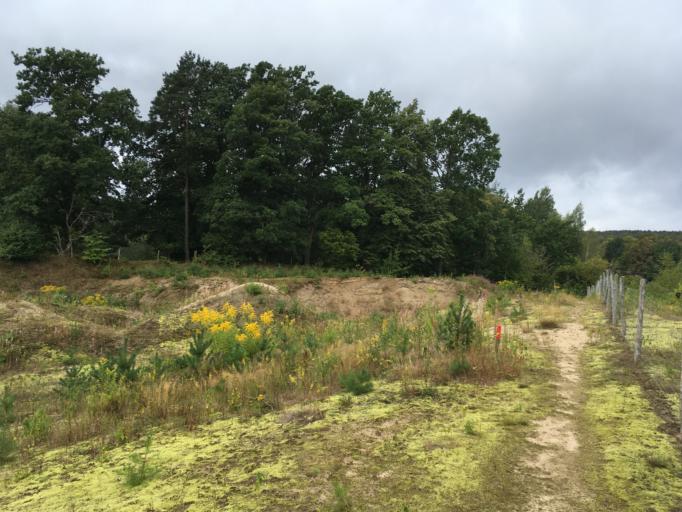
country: SE
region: Blekinge
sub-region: Olofstroms Kommun
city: Jamshog
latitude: 56.2183
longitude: 14.5183
